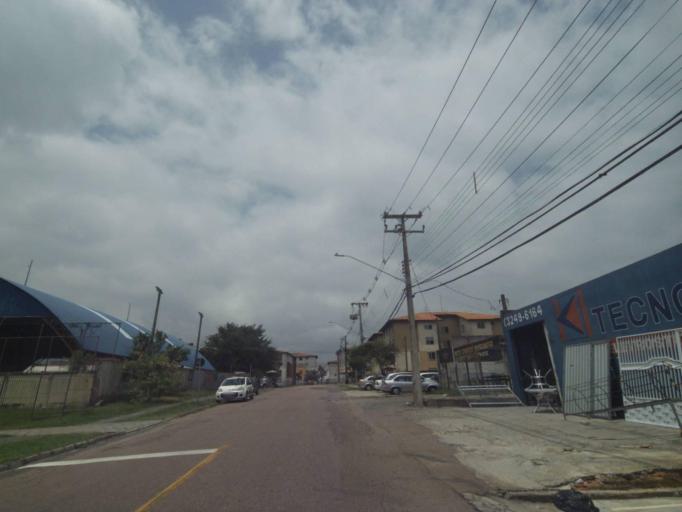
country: BR
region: Parana
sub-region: Curitiba
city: Curitiba
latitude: -25.4934
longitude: -49.3497
